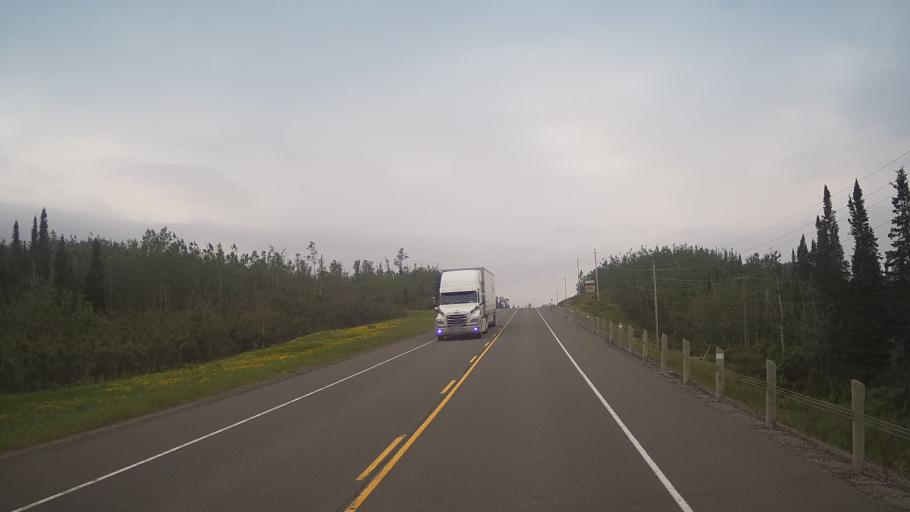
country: CA
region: Ontario
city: Greenstone
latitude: 49.4756
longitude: -88.0922
